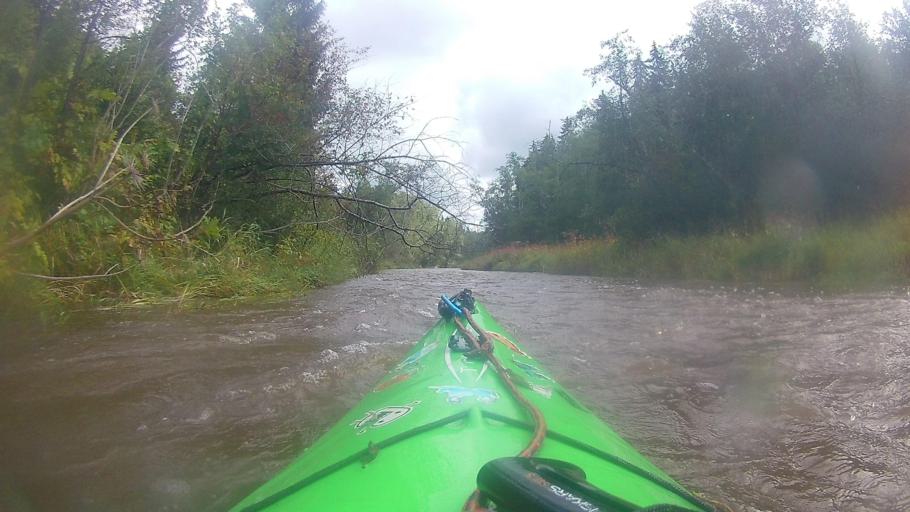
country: LV
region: Talsu Rajons
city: Sabile
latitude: 57.0028
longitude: 22.6103
